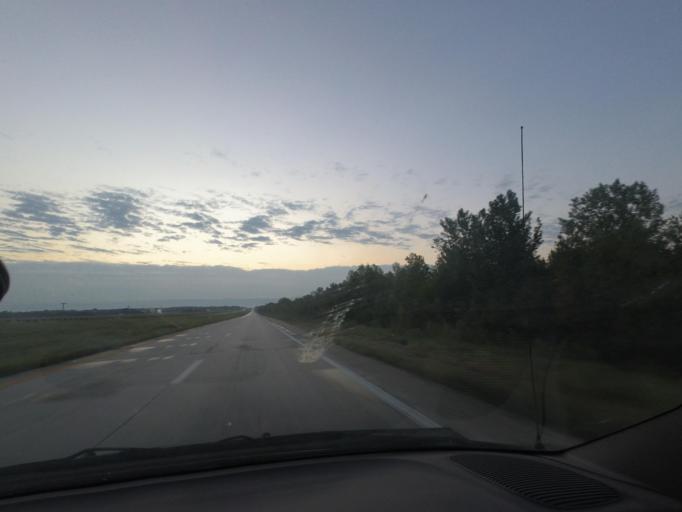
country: US
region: Missouri
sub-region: Macon County
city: Macon
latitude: 39.7601
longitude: -92.6913
